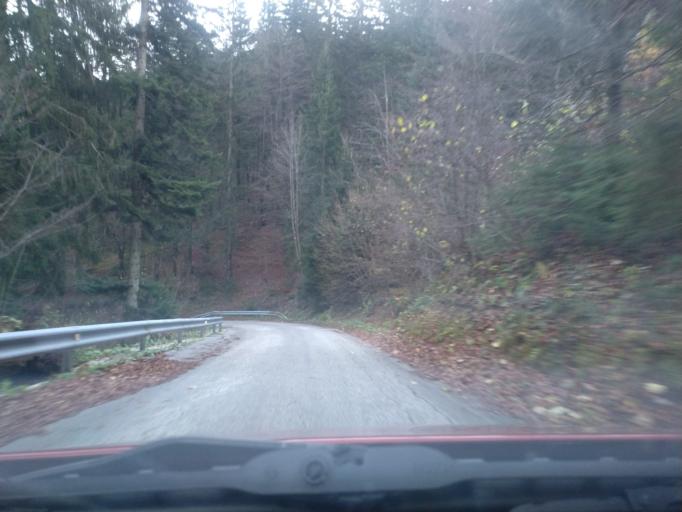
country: SI
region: Kamnik
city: Mekinje
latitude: 46.2848
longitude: 14.6907
